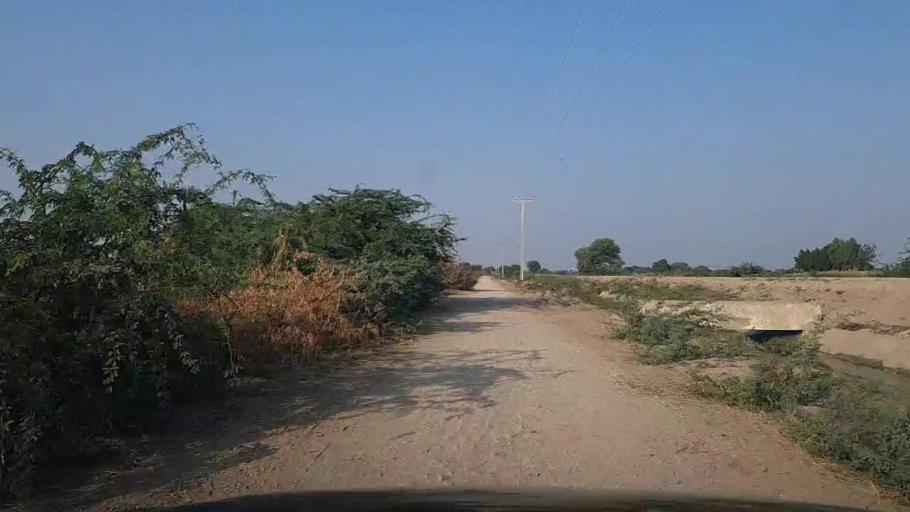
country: PK
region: Sindh
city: Thatta
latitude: 24.7517
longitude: 67.9590
